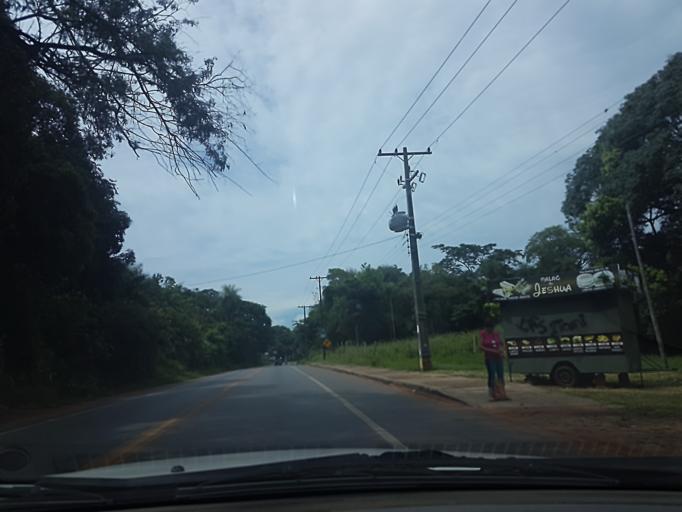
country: PY
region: Central
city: Limpio
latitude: -25.2433
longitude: -57.4581
